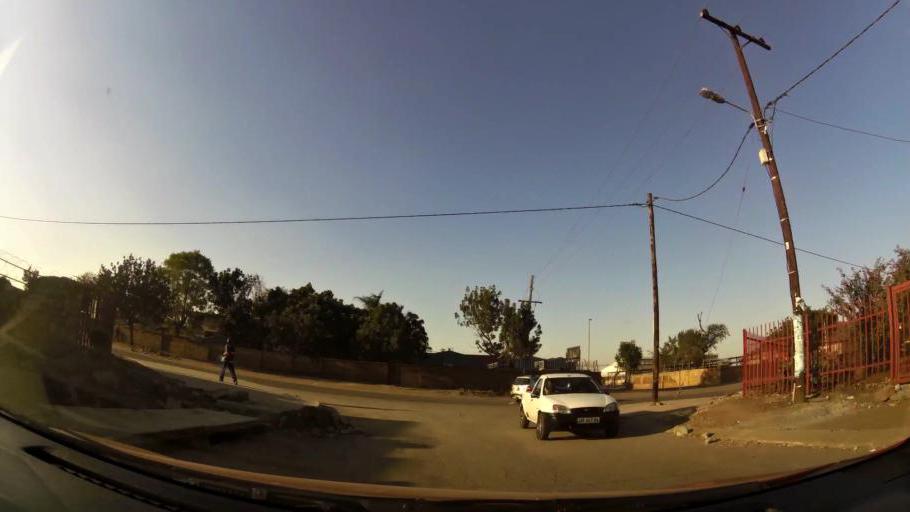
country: ZA
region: North-West
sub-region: Bojanala Platinum District Municipality
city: Rustenburg
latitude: -25.6374
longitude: 27.2218
